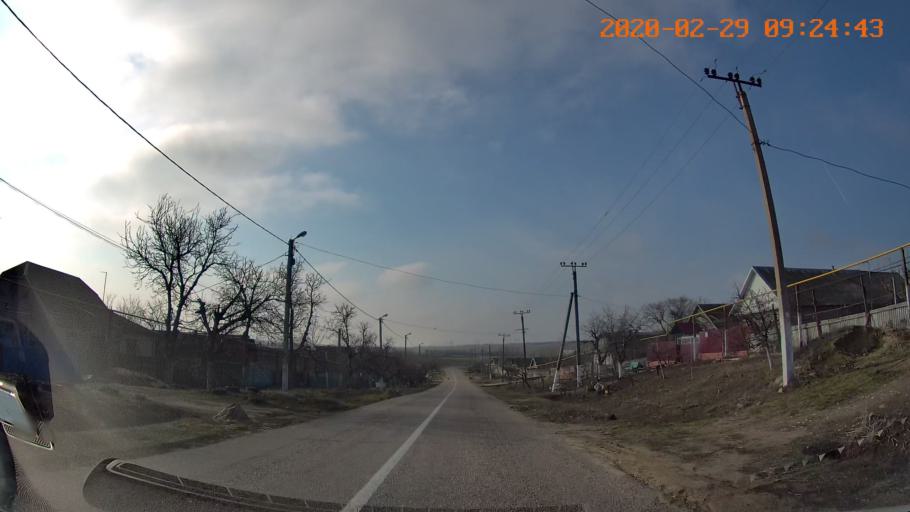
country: MD
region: Telenesti
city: Pervomaisc
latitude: 46.7134
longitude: 29.9578
